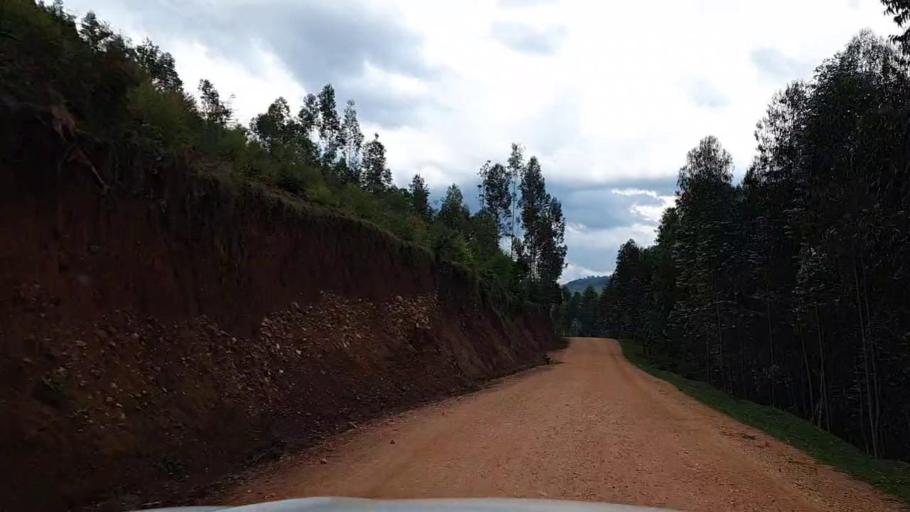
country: RW
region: Southern Province
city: Nyanza
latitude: -2.4048
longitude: 29.6759
